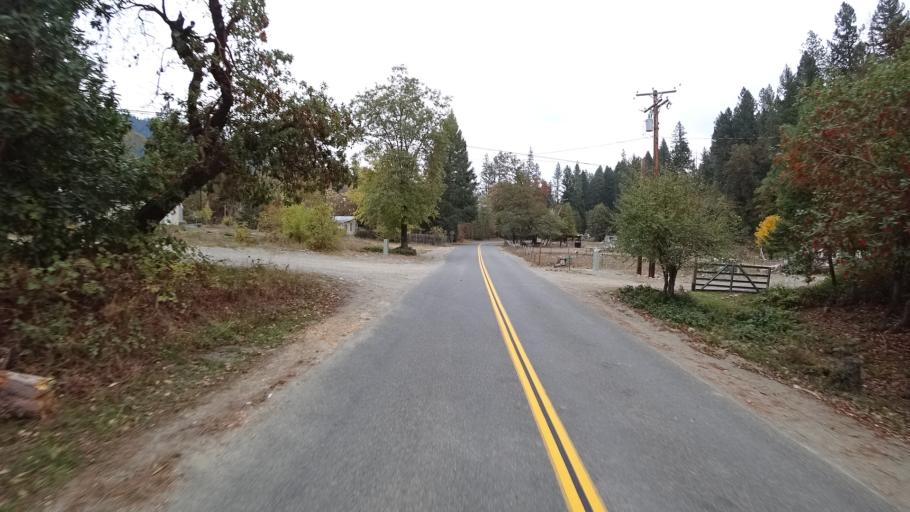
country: US
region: California
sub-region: Siskiyou County
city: Happy Camp
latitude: 41.7836
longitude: -123.3916
